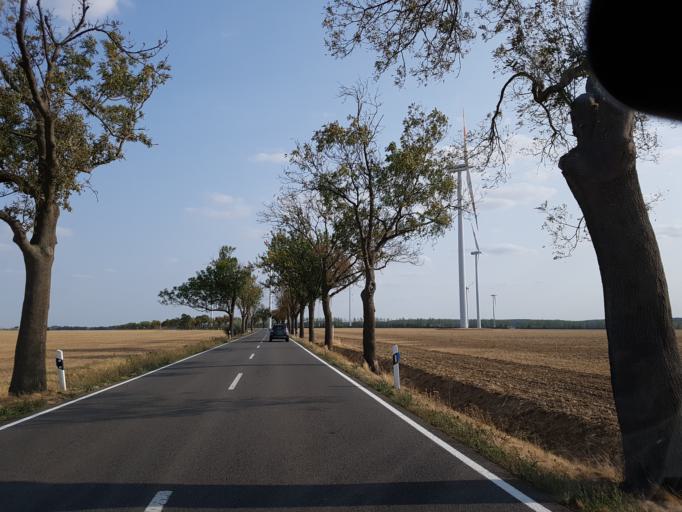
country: DE
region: Saxony-Anhalt
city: Muhlanger
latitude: 51.7784
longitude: 12.7209
